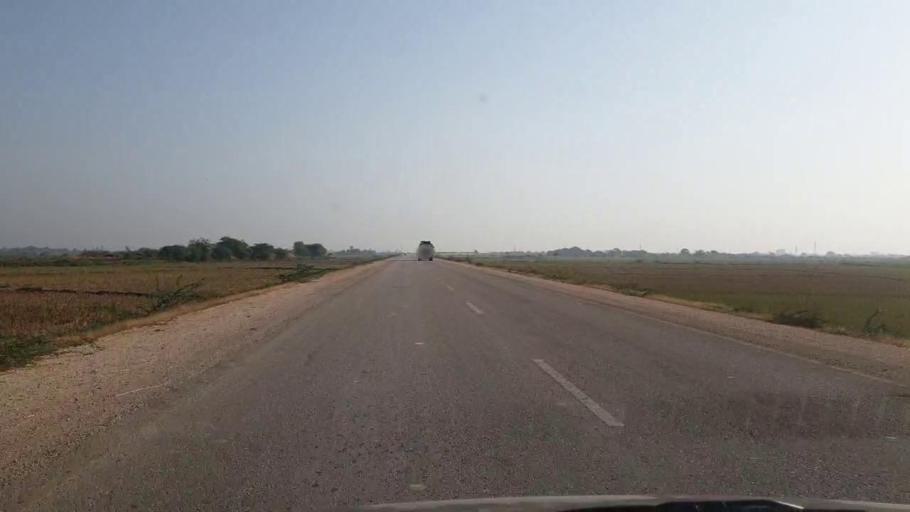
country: PK
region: Sindh
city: Badin
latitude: 24.6743
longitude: 68.8070
